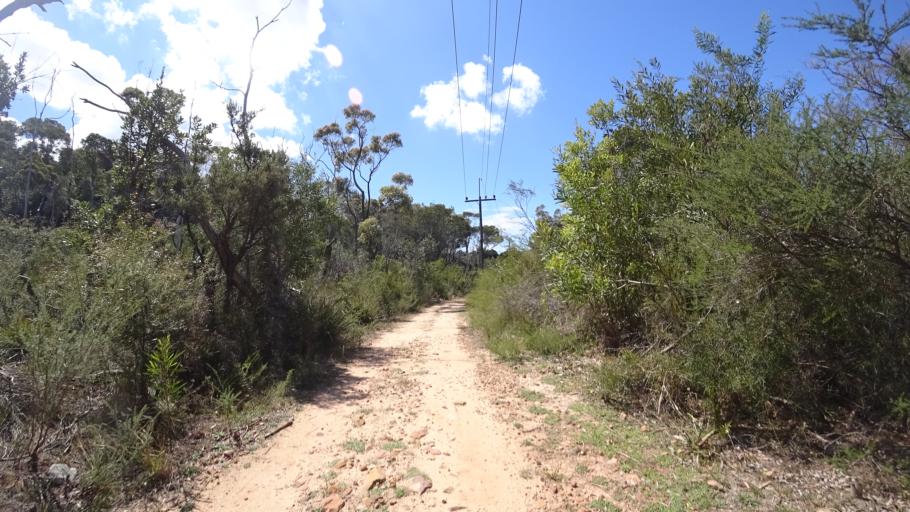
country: AU
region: New South Wales
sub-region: Warringah
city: Killarney Heights
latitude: -33.7624
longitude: 151.2225
